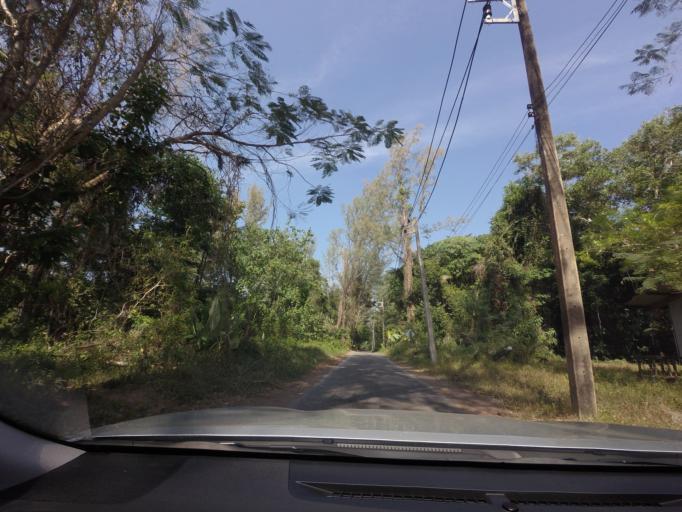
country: TH
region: Phangnga
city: Ban Khao Lak
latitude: 8.7376
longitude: 98.2441
